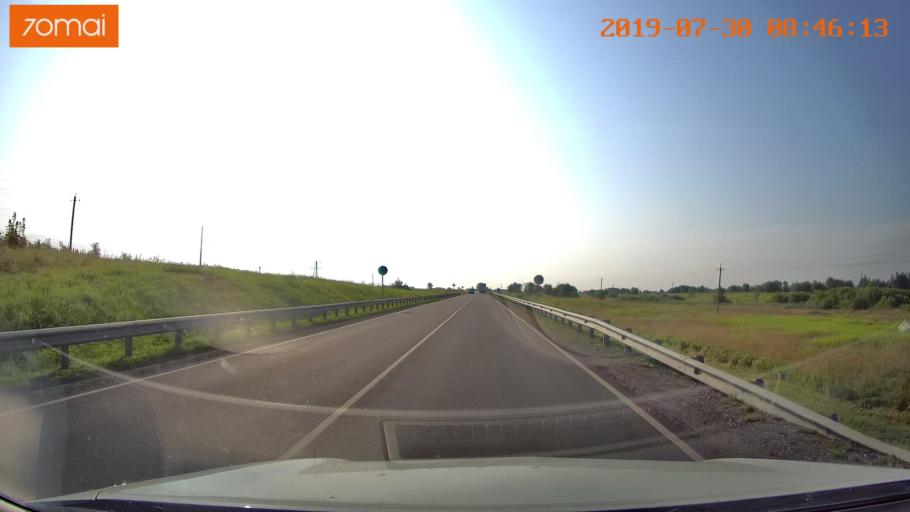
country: RU
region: Kaliningrad
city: Chernyakhovsk
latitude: 54.6245
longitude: 21.8801
